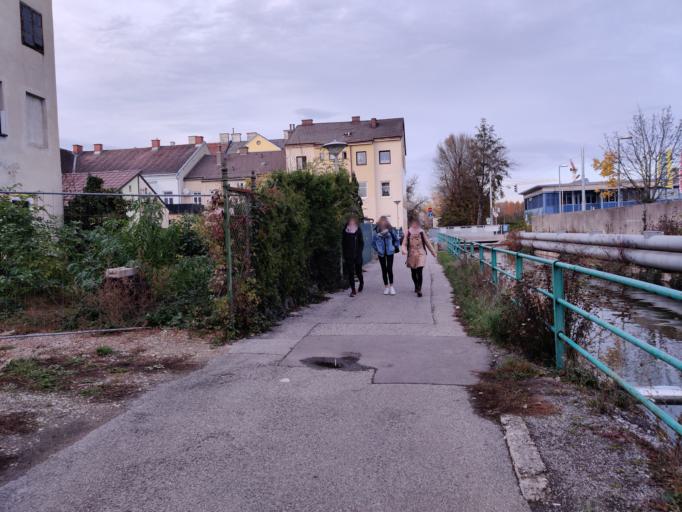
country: AT
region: Lower Austria
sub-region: Sankt Polten Stadt
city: Sankt Poelten
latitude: 48.2093
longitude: 15.6302
